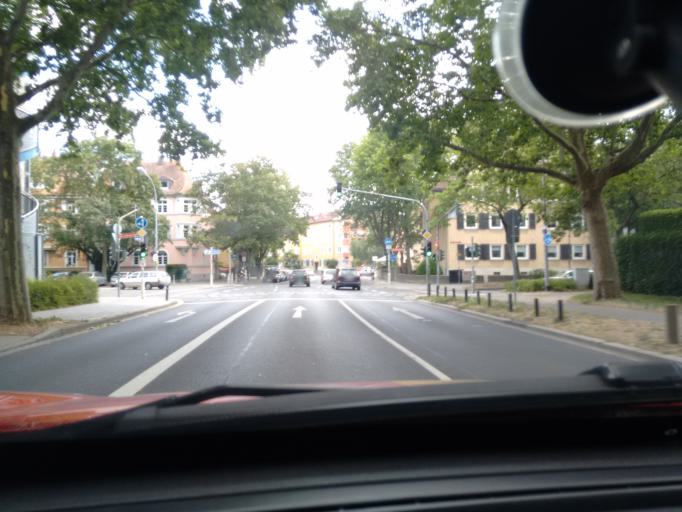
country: DE
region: Rheinland-Pfalz
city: Mainz
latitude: 49.9916
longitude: 8.2615
